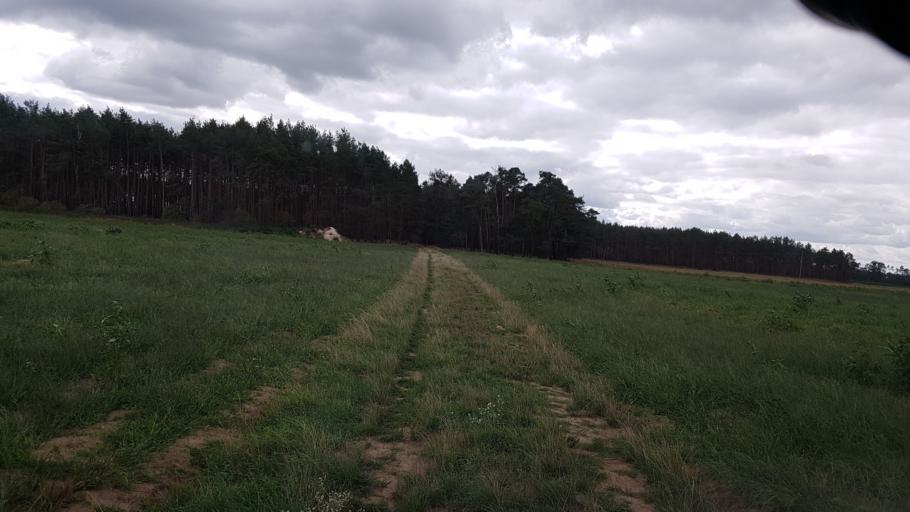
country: DE
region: Brandenburg
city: Schilda
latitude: 51.5531
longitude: 13.3214
